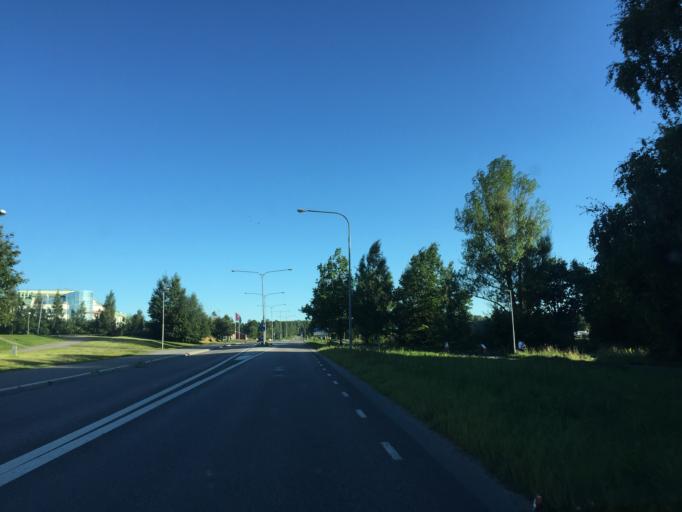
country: SE
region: OErebro
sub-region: Orebro Kommun
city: Orebro
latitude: 59.2575
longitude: 15.1955
